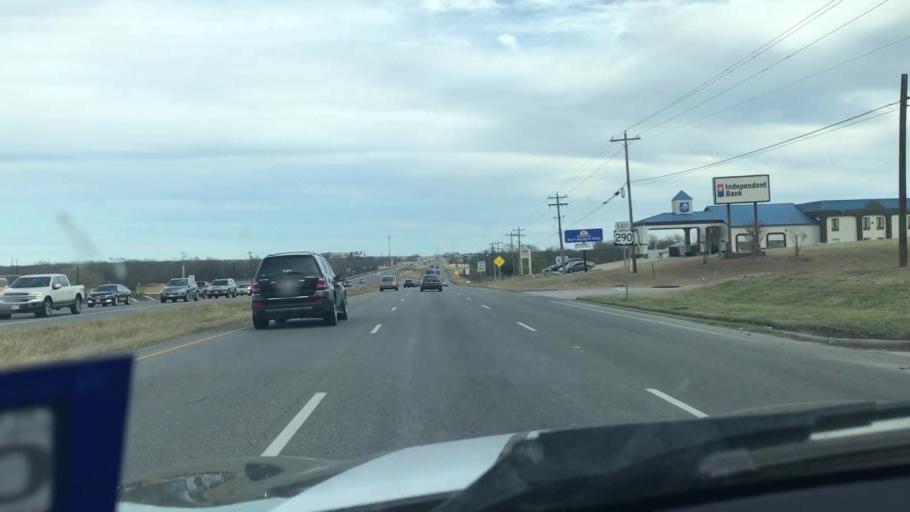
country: US
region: Texas
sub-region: Travis County
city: Manor
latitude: 30.3488
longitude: -97.5553
